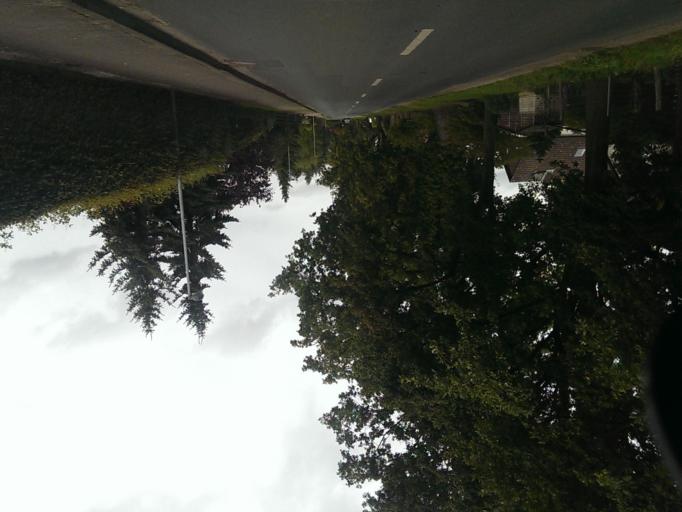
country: DE
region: Lower Saxony
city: Lindwedel
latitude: 52.5514
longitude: 9.6859
